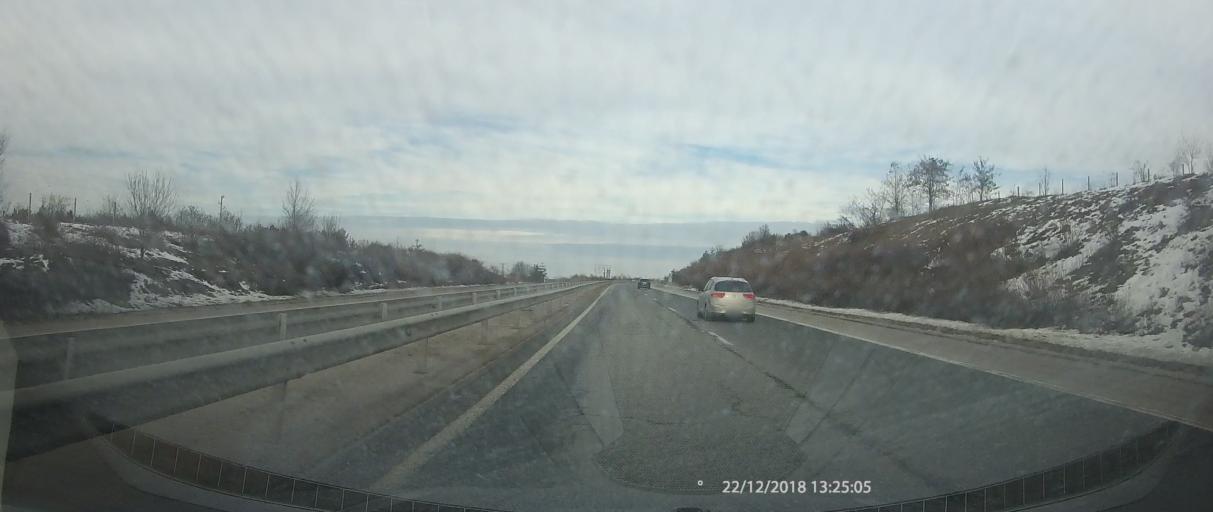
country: BG
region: Lovech
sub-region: Obshtina Yablanitsa
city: Yablanitsa
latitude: 43.0307
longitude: 24.1170
